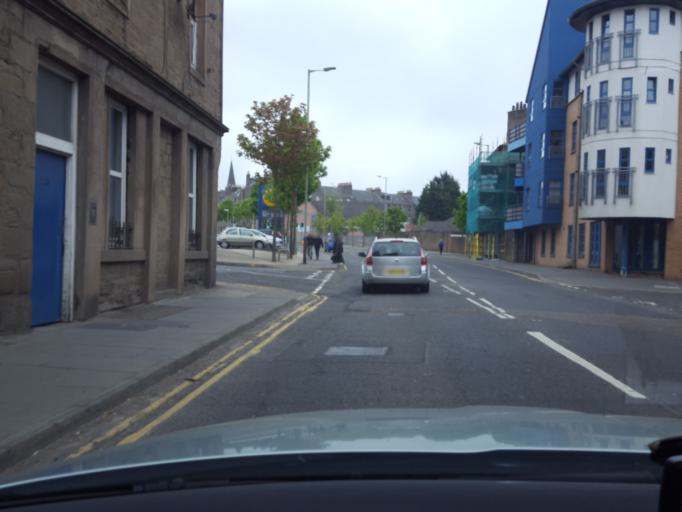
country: GB
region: Scotland
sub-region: Dundee City
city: Dundee
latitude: 56.4704
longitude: -2.9608
